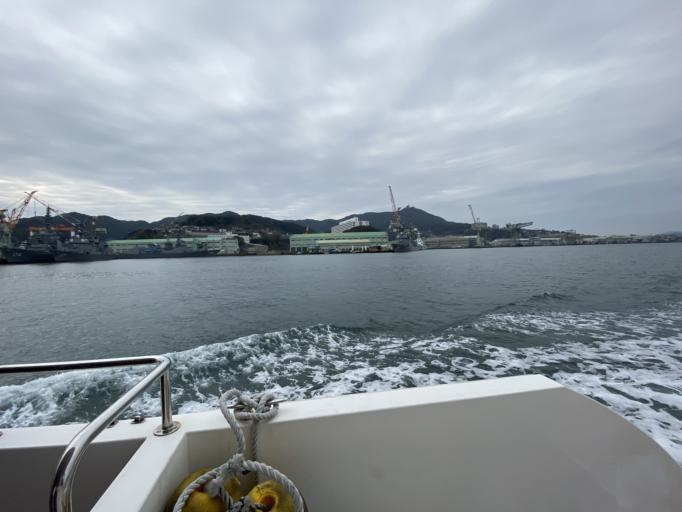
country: JP
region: Nagasaki
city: Nagasaki-shi
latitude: 32.7347
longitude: 129.8607
